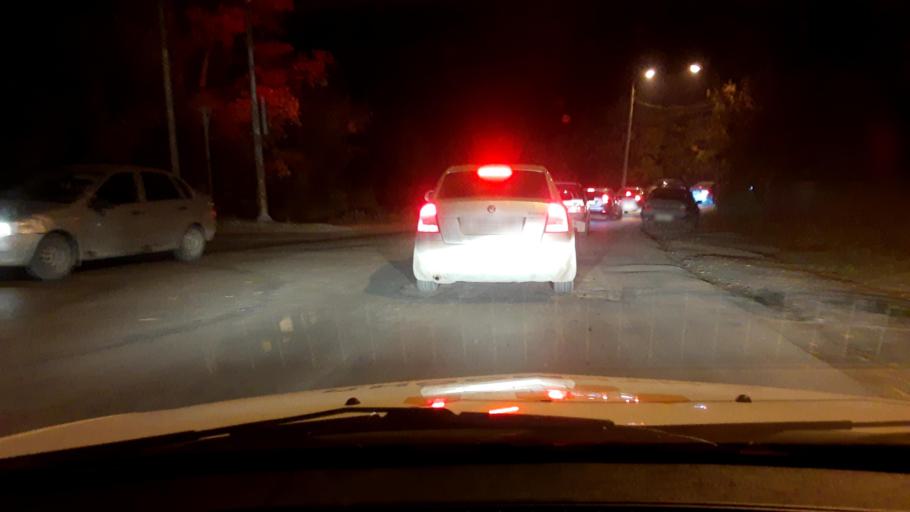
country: RU
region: Bashkortostan
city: Iglino
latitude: 54.7776
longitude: 56.2303
